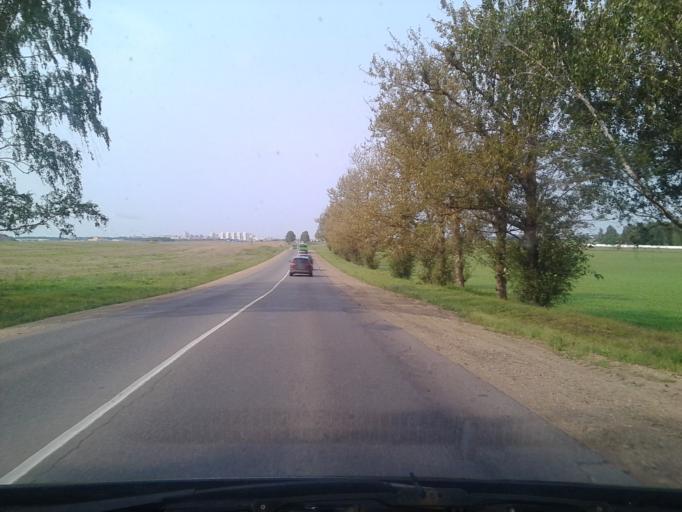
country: BY
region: Minsk
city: Hatava
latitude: 53.8183
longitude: 27.6422
